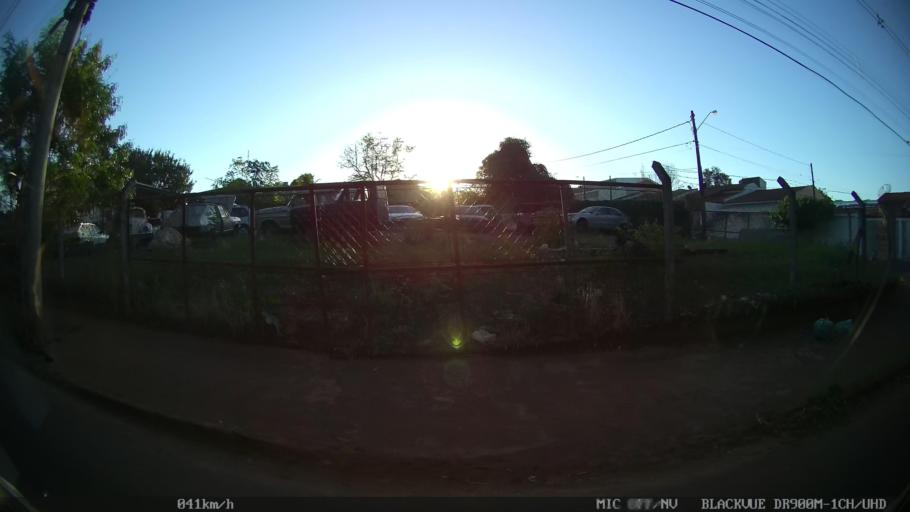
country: BR
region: Sao Paulo
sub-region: Sao Jose Do Rio Preto
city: Sao Jose do Rio Preto
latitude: -20.7774
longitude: -49.3563
